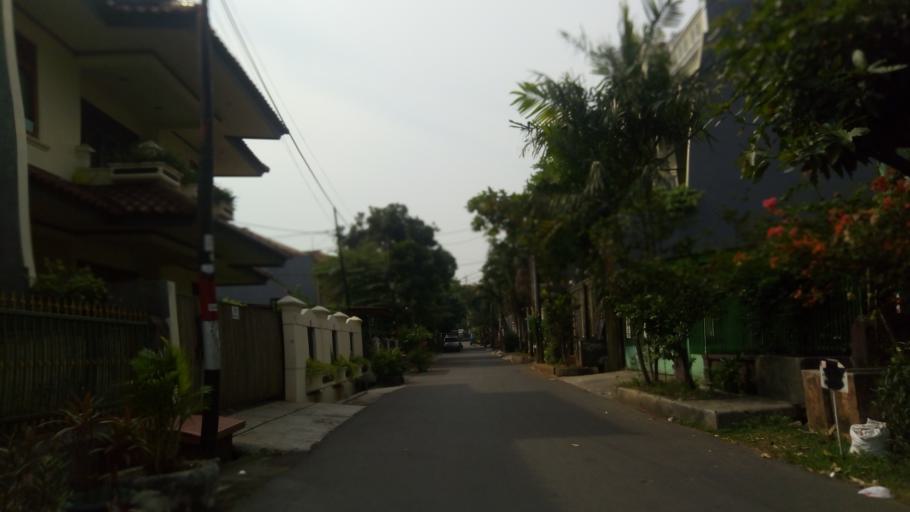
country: ID
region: Jakarta Raya
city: Jakarta
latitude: -6.1714
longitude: 106.8513
